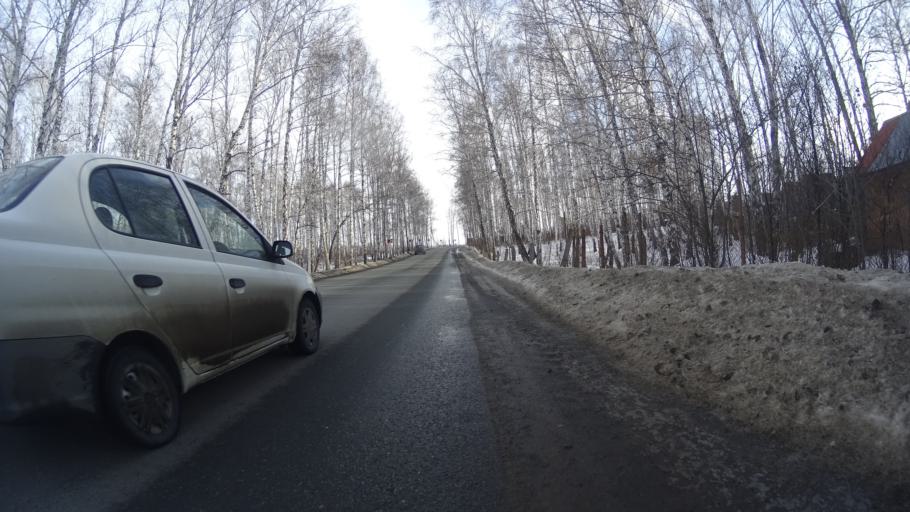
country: RU
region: Chelyabinsk
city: Sargazy
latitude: 55.1266
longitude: 61.2889
